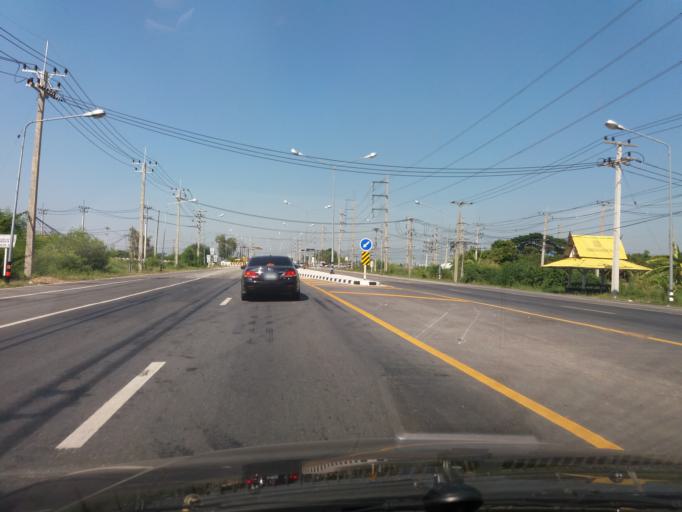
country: TH
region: Chai Nat
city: Manorom
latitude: 15.2993
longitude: 100.1000
